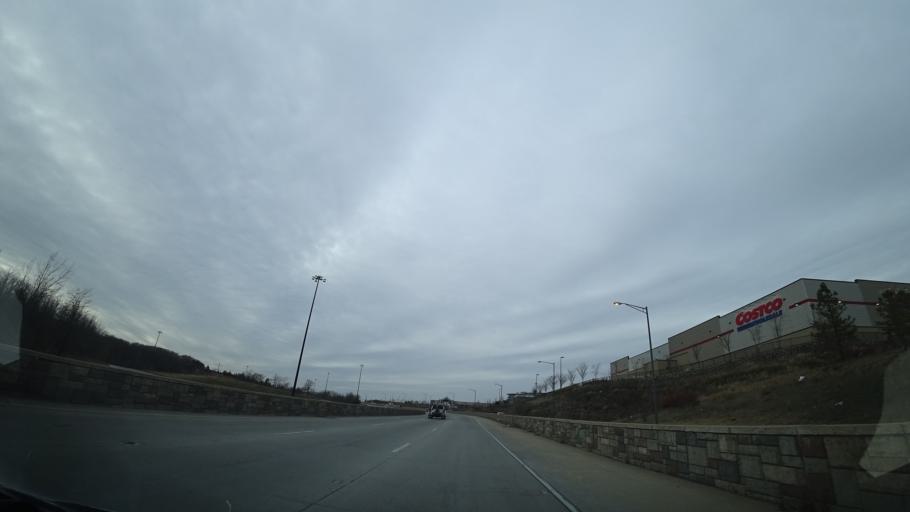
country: US
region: Maryland
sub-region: Prince George's County
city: Colmar Manor
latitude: 38.9187
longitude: -76.9520
